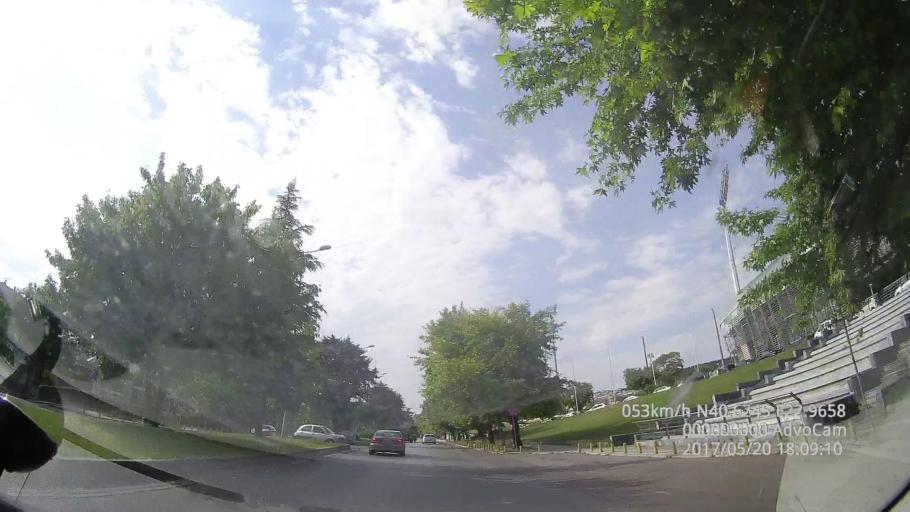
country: GR
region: Central Macedonia
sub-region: Nomos Thessalonikis
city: Triandria
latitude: 40.6248
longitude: 22.9655
